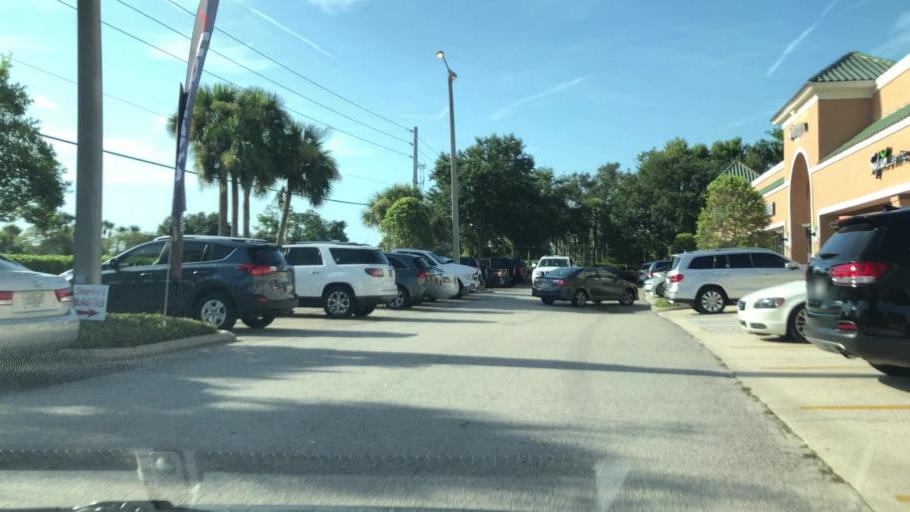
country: US
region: Florida
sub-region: Saint Johns County
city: Sawgrass
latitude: 30.1887
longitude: -81.3802
